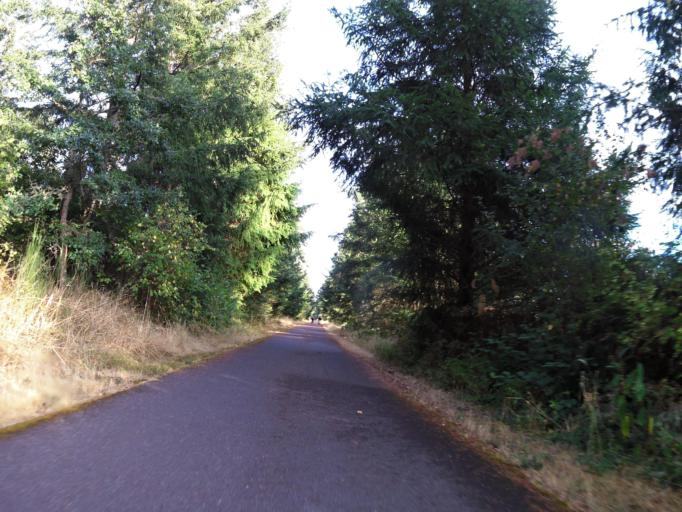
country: US
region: Washington
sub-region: Thurston County
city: Rainier
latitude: 46.8807
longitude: -122.7361
